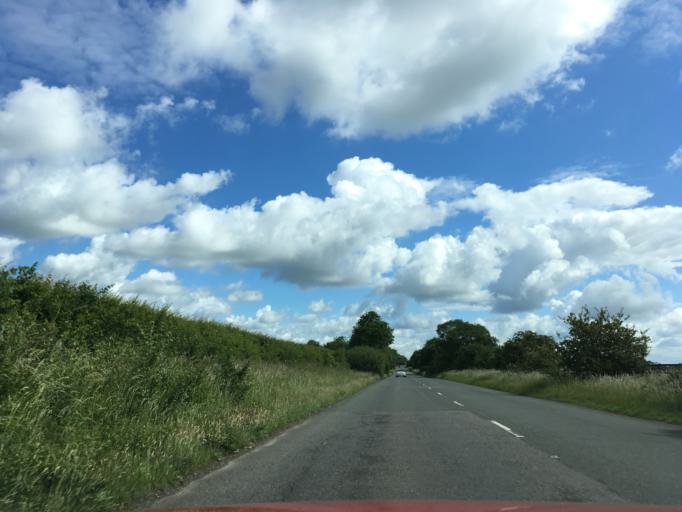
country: GB
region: England
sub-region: Gloucestershire
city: Lechlade
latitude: 51.7425
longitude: -1.6582
